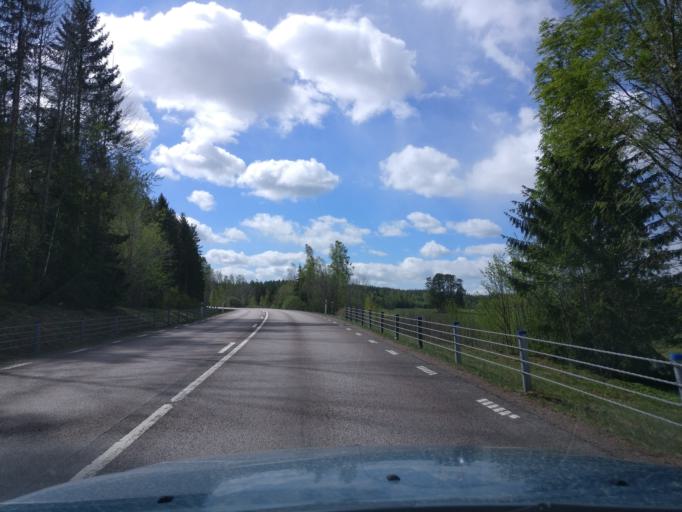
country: SE
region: Vaermland
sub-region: Karlstads Kommun
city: Molkom
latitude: 59.5414
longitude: 13.6233
